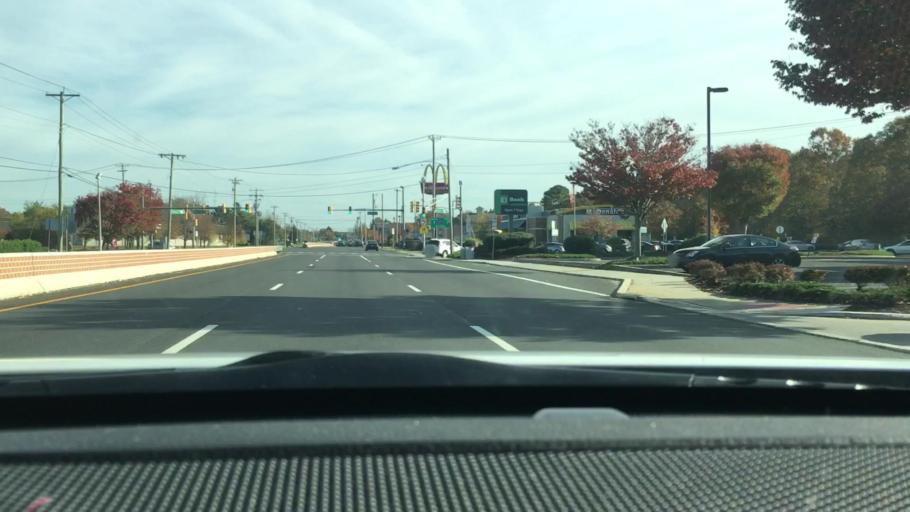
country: US
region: New Jersey
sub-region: Atlantic County
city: Absecon
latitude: 39.4325
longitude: -74.5120
